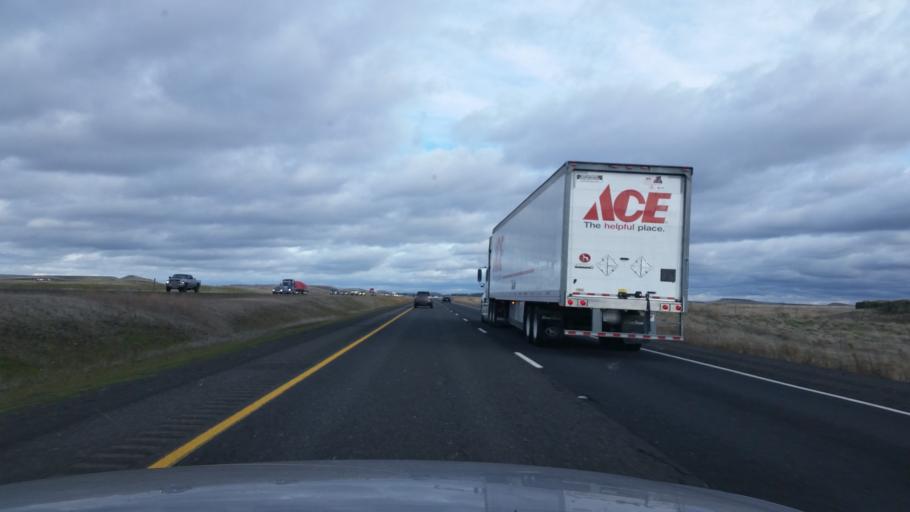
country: US
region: Washington
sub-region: Spokane County
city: Medical Lake
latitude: 47.3269
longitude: -117.9321
